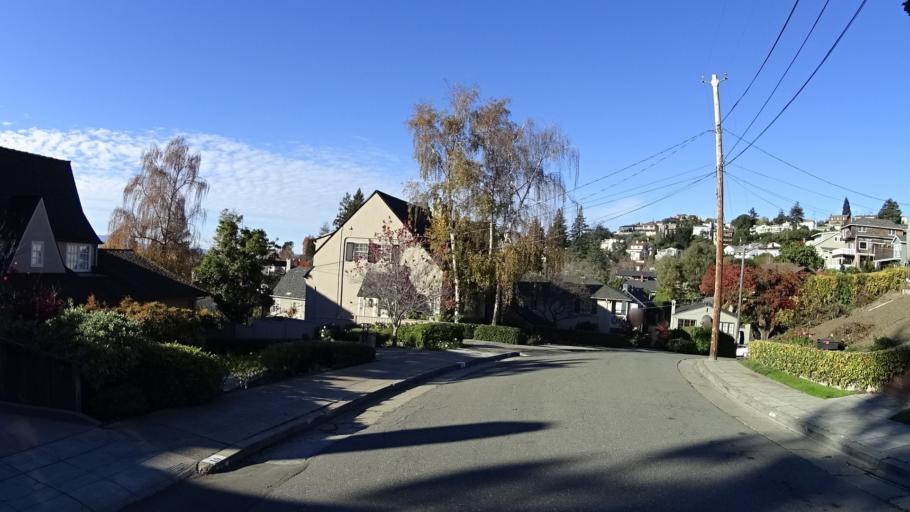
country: US
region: California
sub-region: Alameda County
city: Piedmont
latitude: 37.8251
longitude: -122.2280
